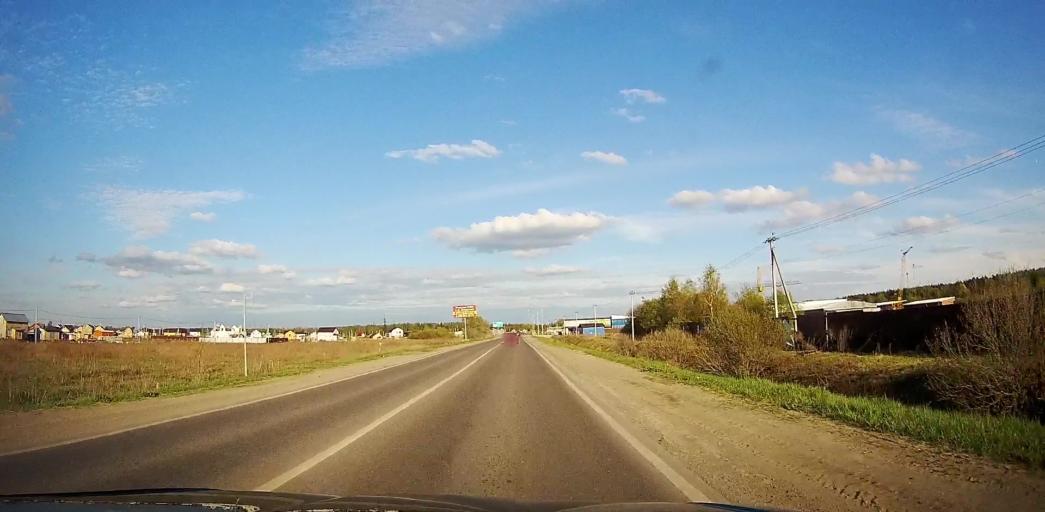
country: RU
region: Moskovskaya
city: Malyshevo
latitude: 55.4855
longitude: 38.3324
